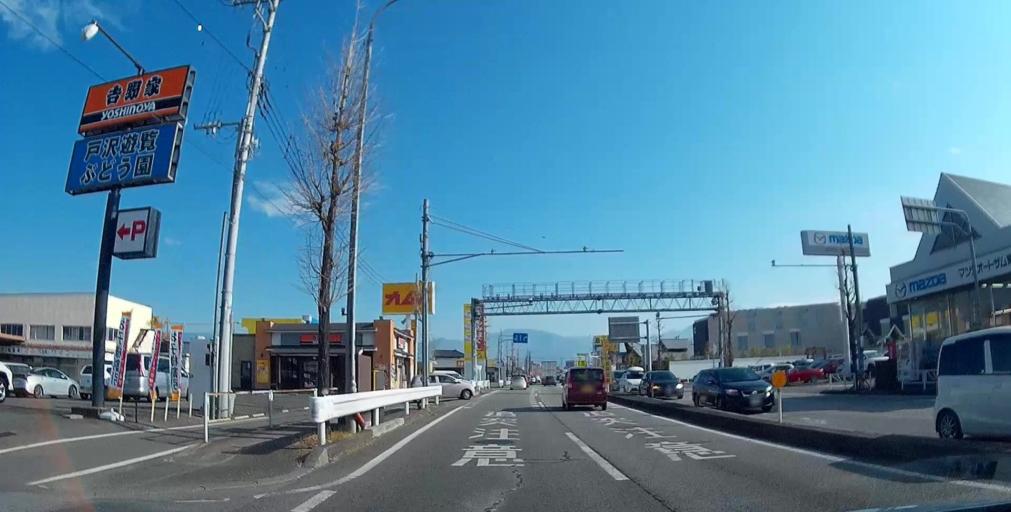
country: JP
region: Yamanashi
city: Isawa
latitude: 35.6461
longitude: 138.6134
